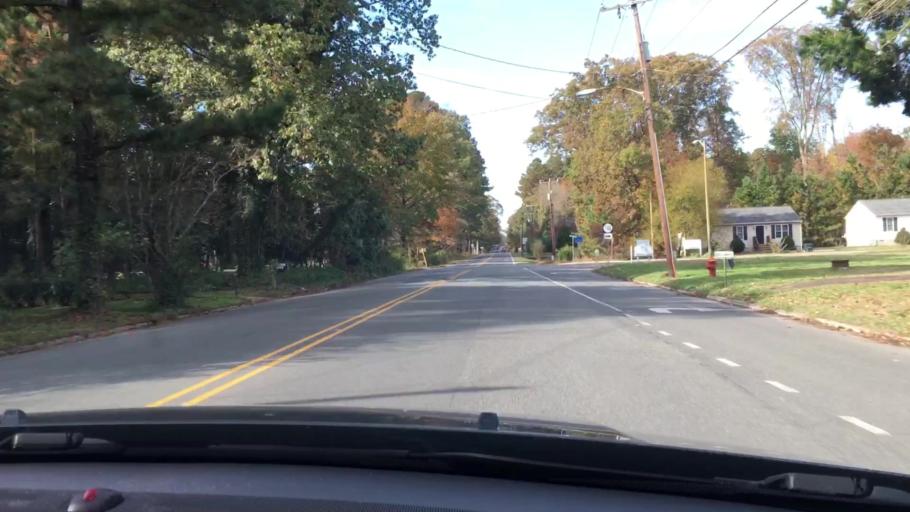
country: US
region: Virginia
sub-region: King William County
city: West Point
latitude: 37.5596
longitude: -76.8212
